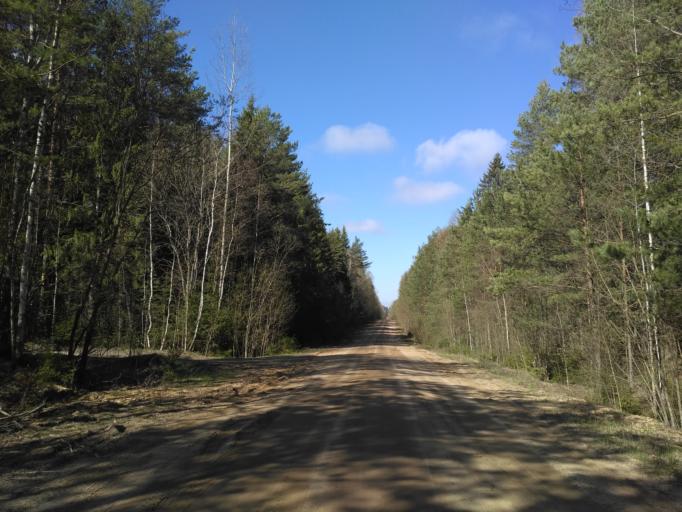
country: BY
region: Minsk
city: Loshnitsa
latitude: 54.4406
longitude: 28.6850
